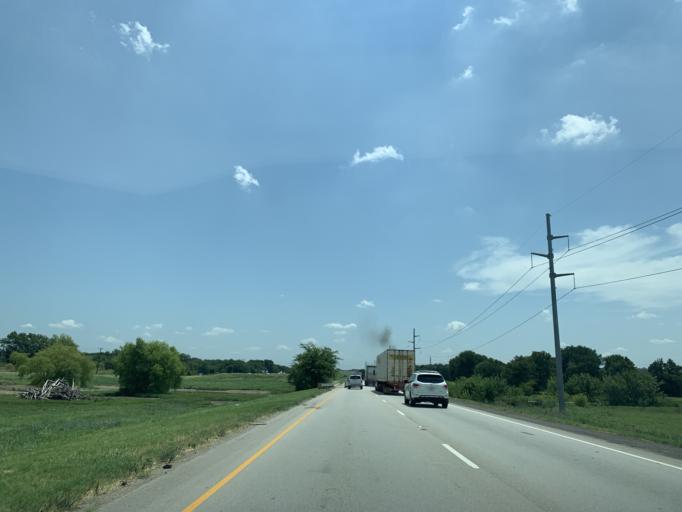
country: US
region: Texas
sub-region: Denton County
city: Roanoke
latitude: 33.0227
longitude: -97.2561
